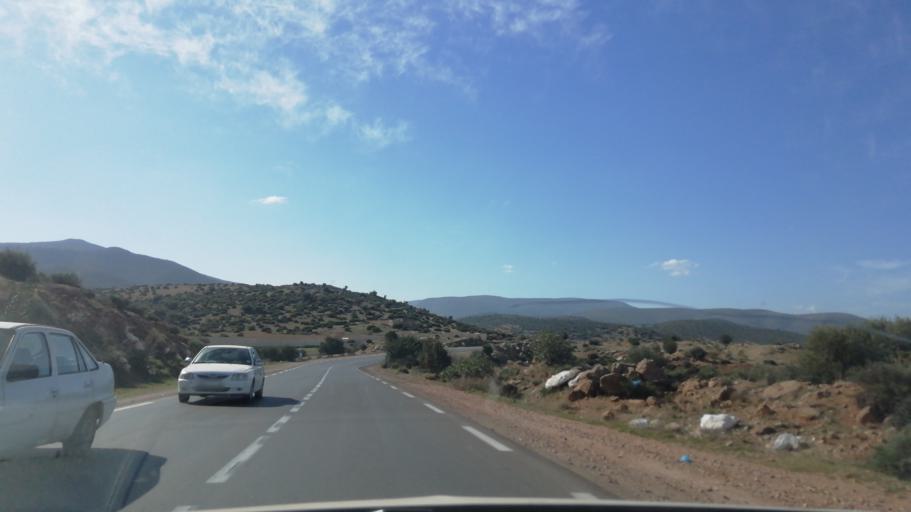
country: DZ
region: Tlemcen
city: Ouled Mimoun
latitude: 34.8703
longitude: -1.1274
